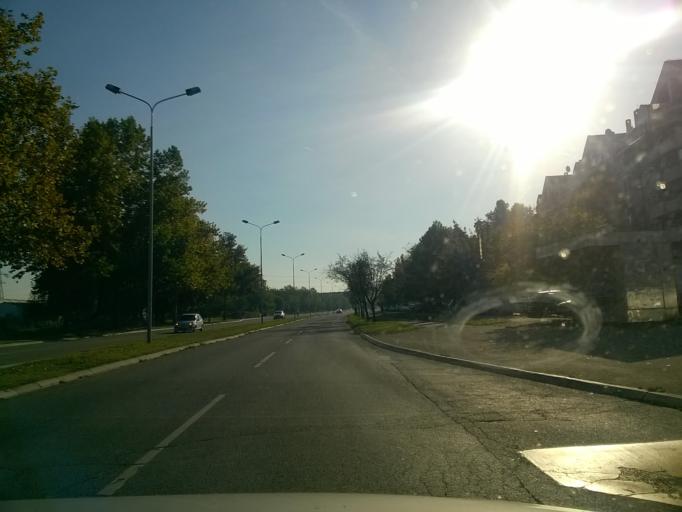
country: RS
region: Central Serbia
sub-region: Belgrade
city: Zemun
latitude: 44.8200
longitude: 20.3799
